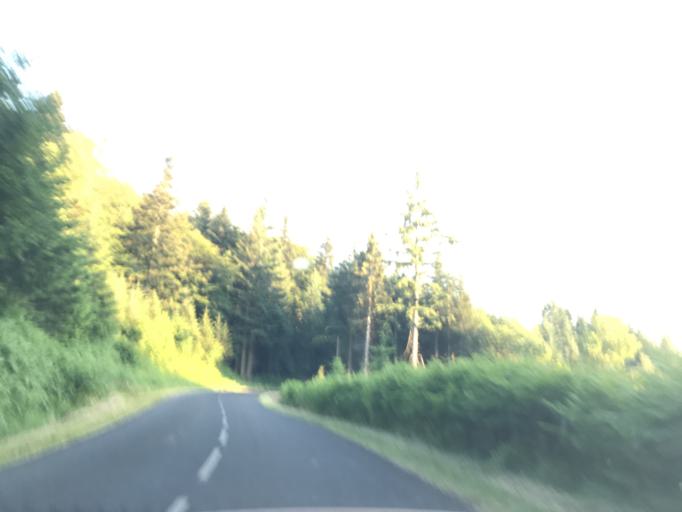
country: FR
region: Auvergne
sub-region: Departement du Puy-de-Dome
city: Celles-sur-Durolle
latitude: 45.7598
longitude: 3.6683
